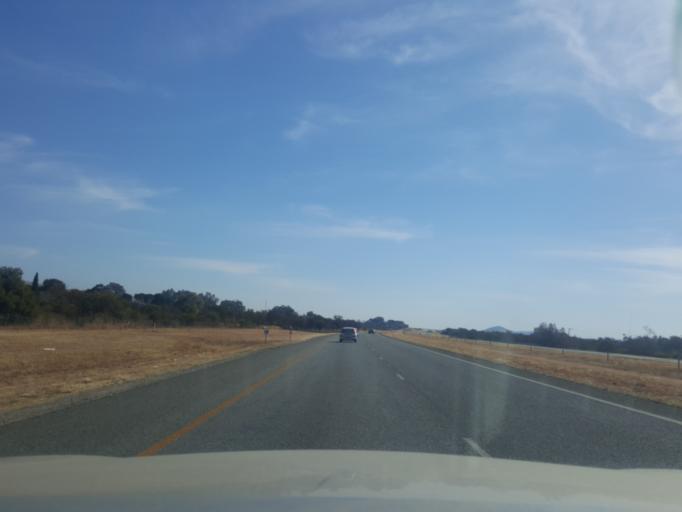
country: ZA
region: North-West
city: Ga-Rankuwa
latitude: -25.6582
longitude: 28.0685
